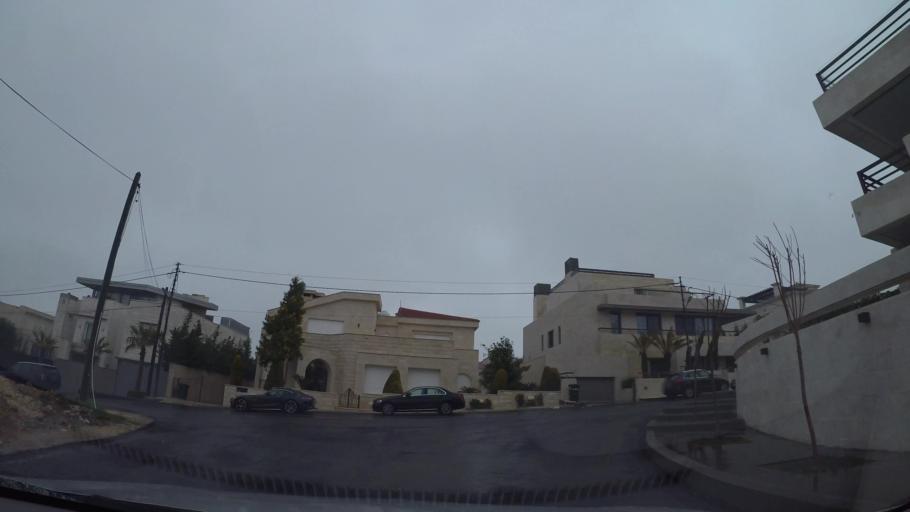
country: JO
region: Amman
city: Al Jubayhah
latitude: 32.0068
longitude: 35.8254
